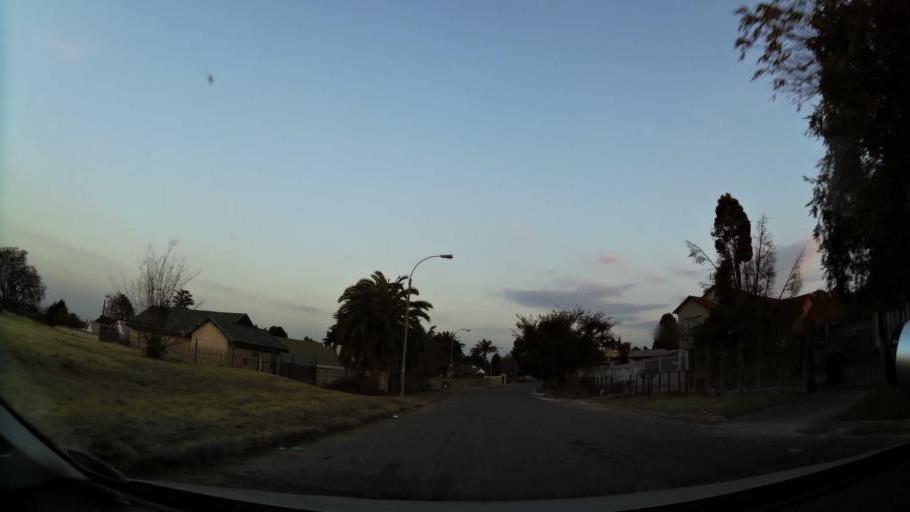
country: ZA
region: Gauteng
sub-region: Ekurhuleni Metropolitan Municipality
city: Tembisa
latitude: -26.0558
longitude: 28.2406
